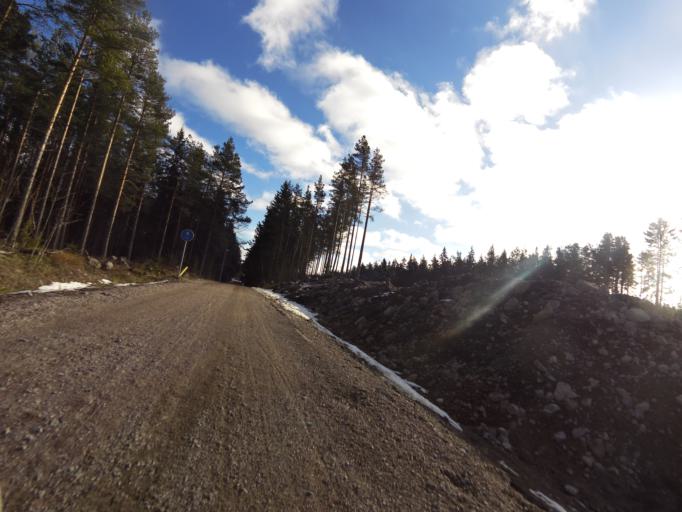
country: SE
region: Uppsala
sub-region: Alvkarleby Kommun
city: Skutskaer
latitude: 60.6503
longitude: 17.3462
